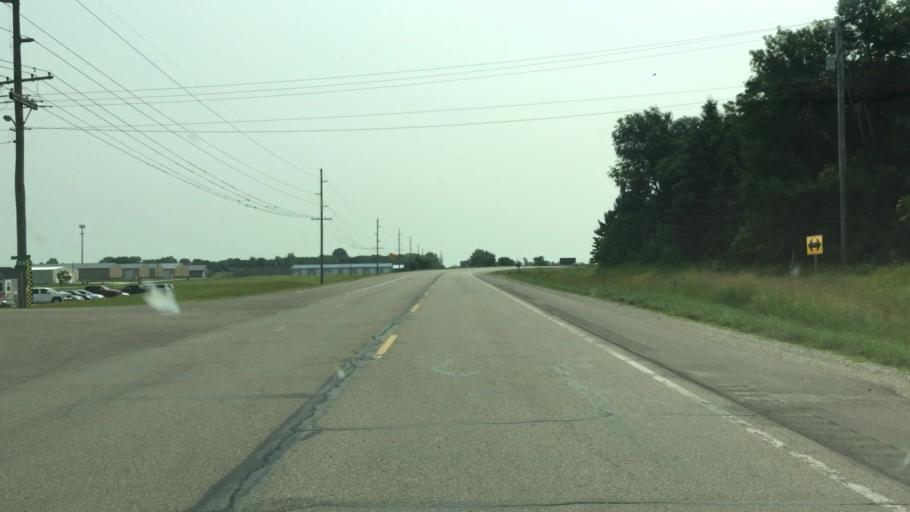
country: US
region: Iowa
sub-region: Dickinson County
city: Milford
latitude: 43.3424
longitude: -95.1601
